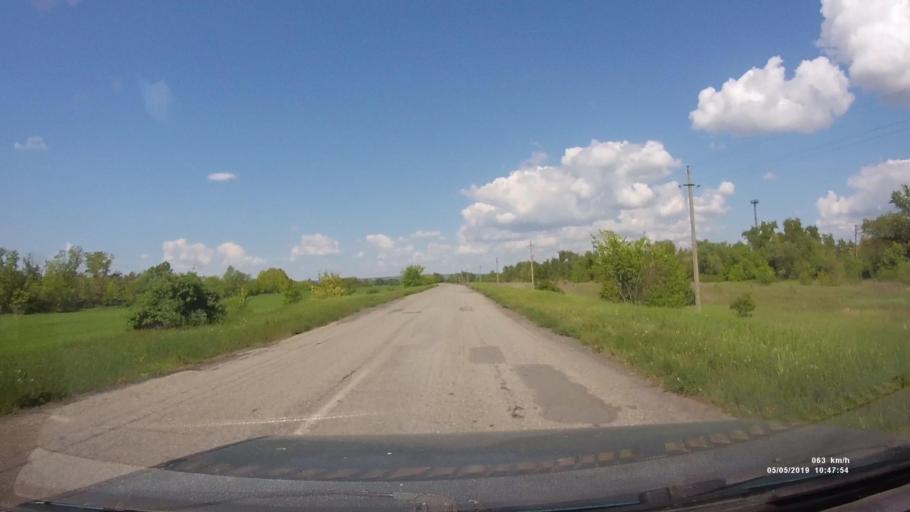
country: RU
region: Rostov
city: Ust'-Donetskiy
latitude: 47.6403
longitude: 40.8268
